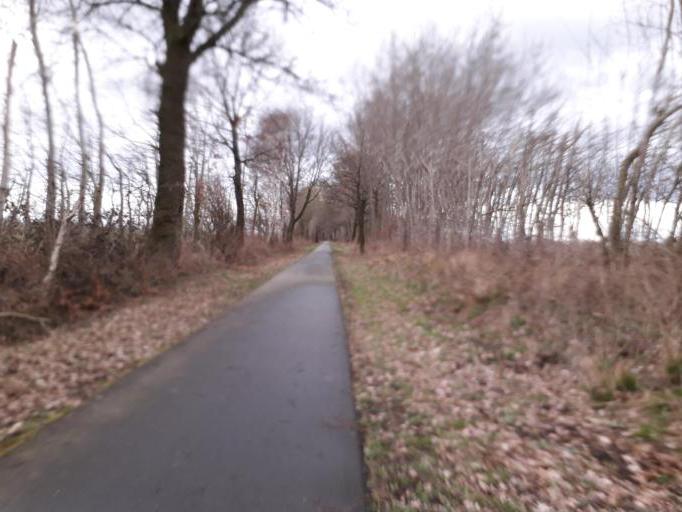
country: DE
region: Schleswig-Holstein
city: Stapelfeld
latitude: 53.5706
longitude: 10.2234
